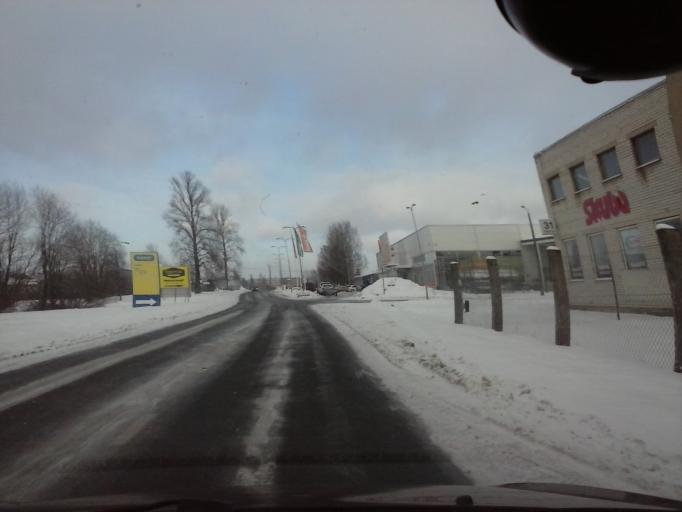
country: EE
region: Viljandimaa
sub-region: Viljandi linn
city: Viljandi
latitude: 58.3518
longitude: 25.5710
